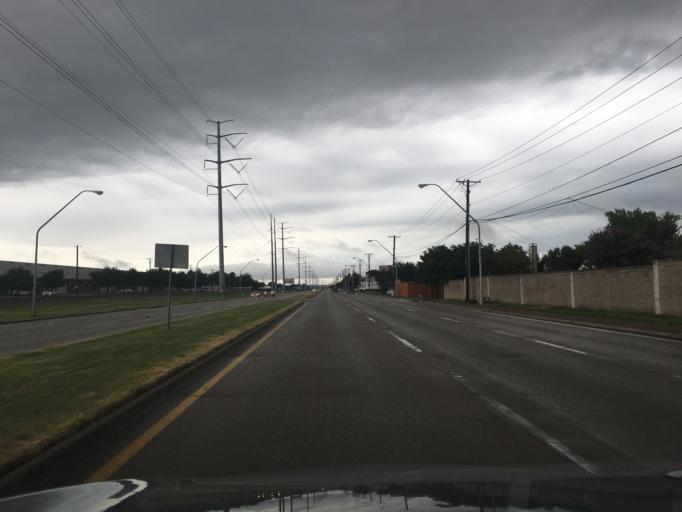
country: US
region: Texas
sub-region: Dallas County
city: Garland
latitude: 32.9336
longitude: -96.6248
